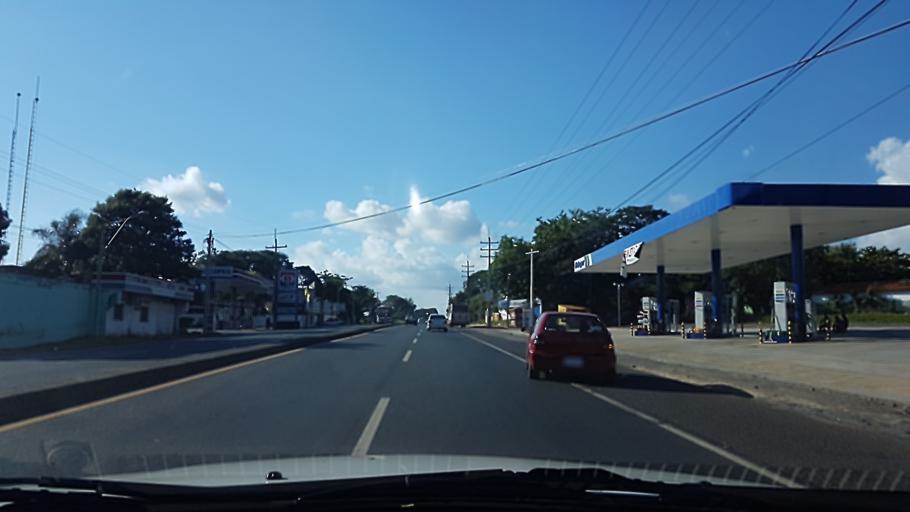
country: PY
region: Central
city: San Antonio
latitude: -25.4405
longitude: -57.5360
